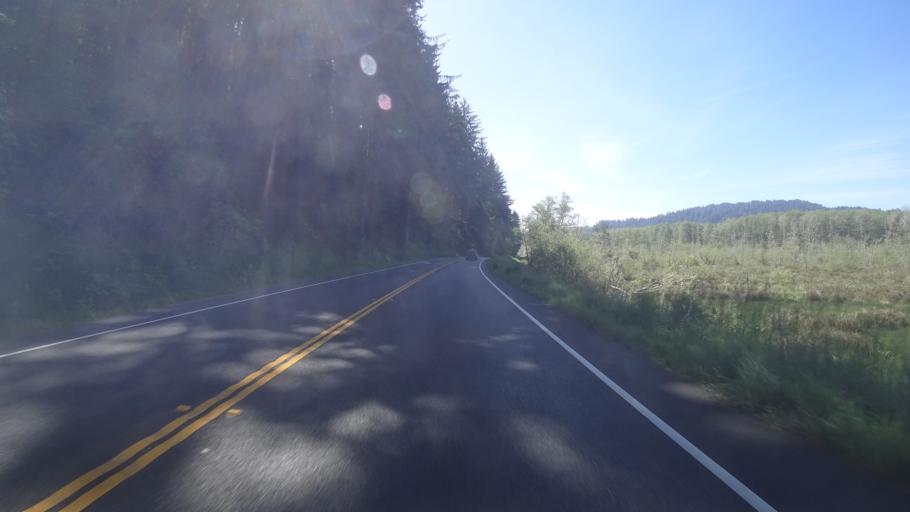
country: US
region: California
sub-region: Del Norte County
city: Bertsch-Oceanview
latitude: 41.5504
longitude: -124.0533
